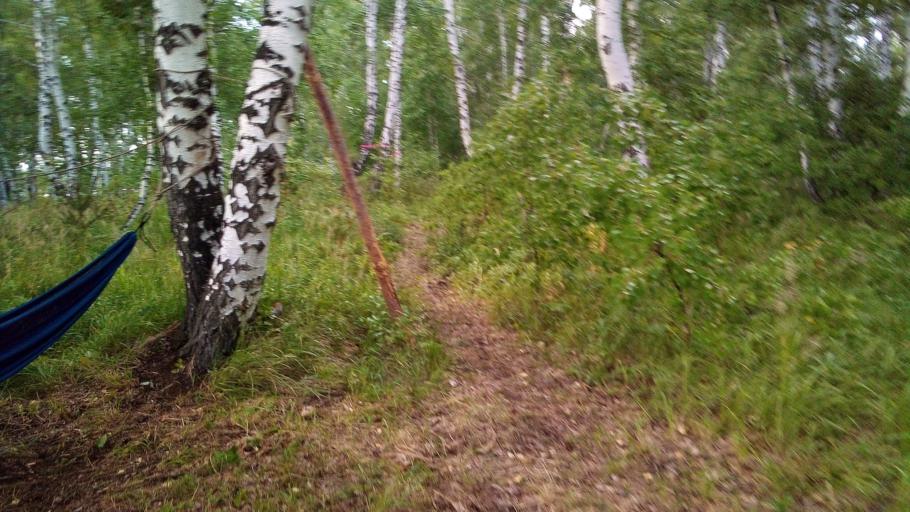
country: RU
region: Chelyabinsk
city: Roshchino
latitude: 55.2592
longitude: 61.0919
